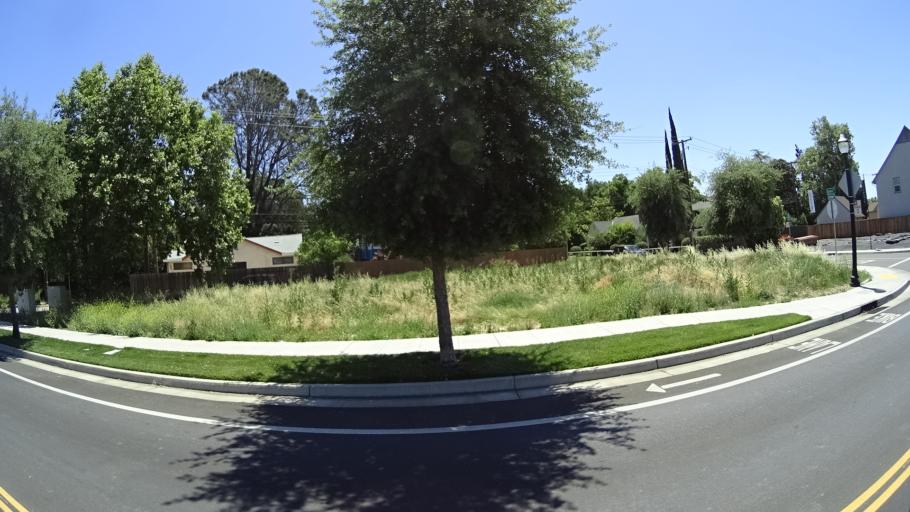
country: US
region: California
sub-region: Sacramento County
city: Sacramento
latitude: 38.5483
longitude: -121.4840
